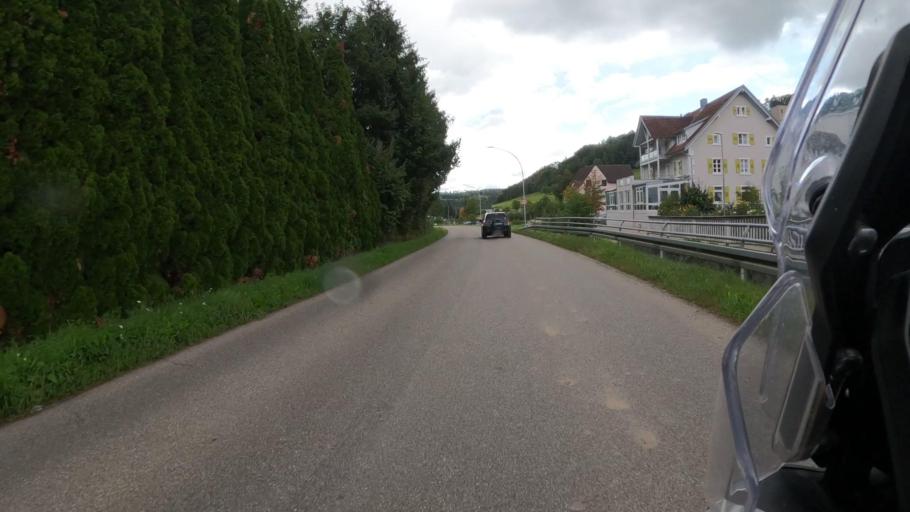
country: DE
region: Baden-Wuerttemberg
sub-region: Freiburg Region
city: Eggingen
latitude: 47.7008
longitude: 8.3870
